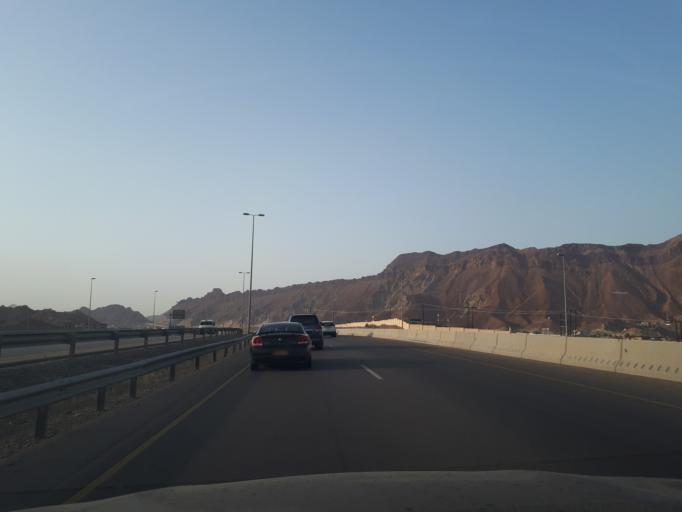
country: OM
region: Muhafazat ad Dakhiliyah
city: Bidbid
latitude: 23.4325
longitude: 58.1207
